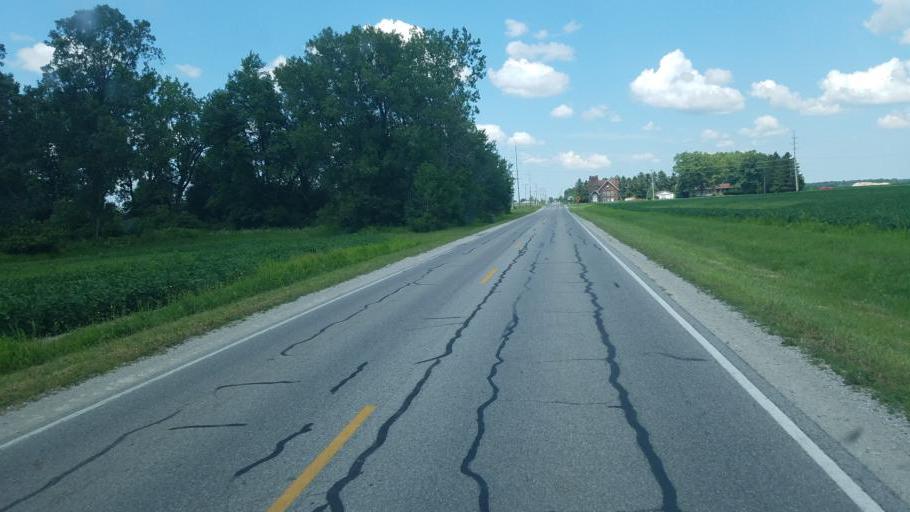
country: US
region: Ohio
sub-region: Marion County
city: Marion
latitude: 40.6277
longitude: -83.0733
